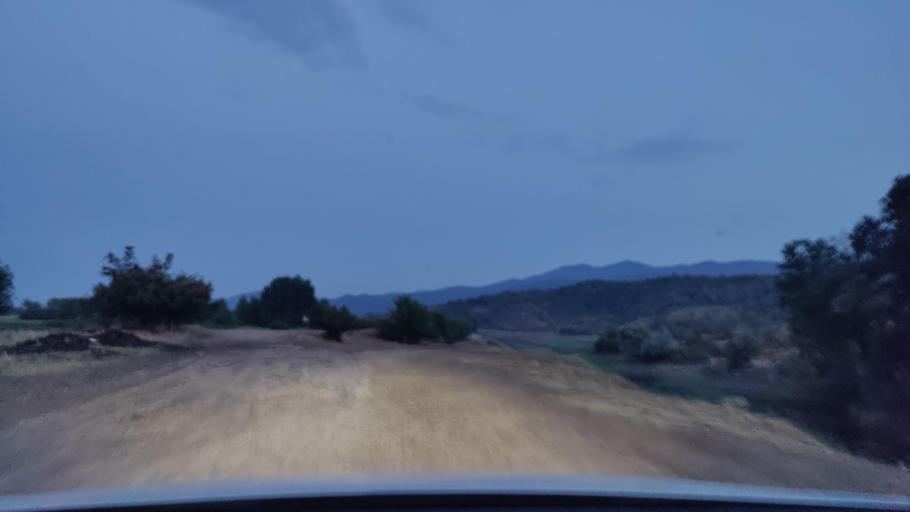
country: GR
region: Central Macedonia
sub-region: Nomos Serron
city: Chrysochorafa
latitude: 41.2050
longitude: 23.0771
